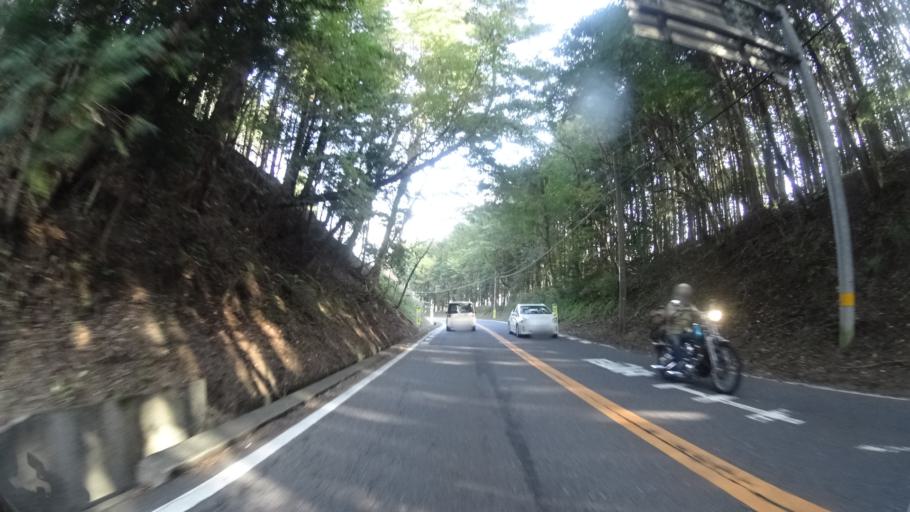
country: JP
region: Oita
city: Tsukawaki
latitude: 33.2613
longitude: 131.3262
